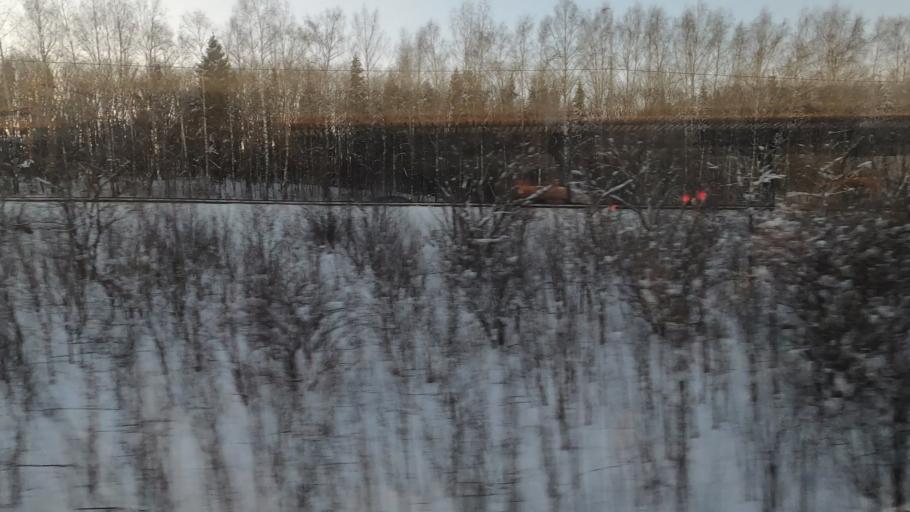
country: RU
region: Moskovskaya
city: Iksha
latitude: 56.1843
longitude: 37.5182
